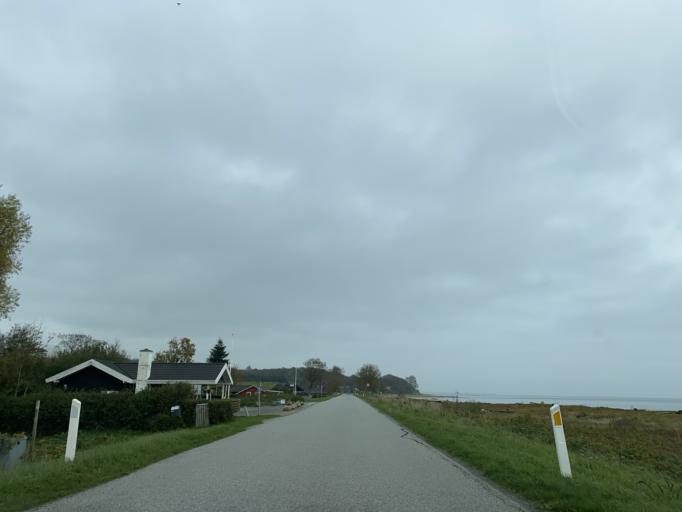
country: DK
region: South Denmark
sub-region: Aabenraa Kommune
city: Lojt Kirkeby
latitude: 55.1578
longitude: 9.4995
